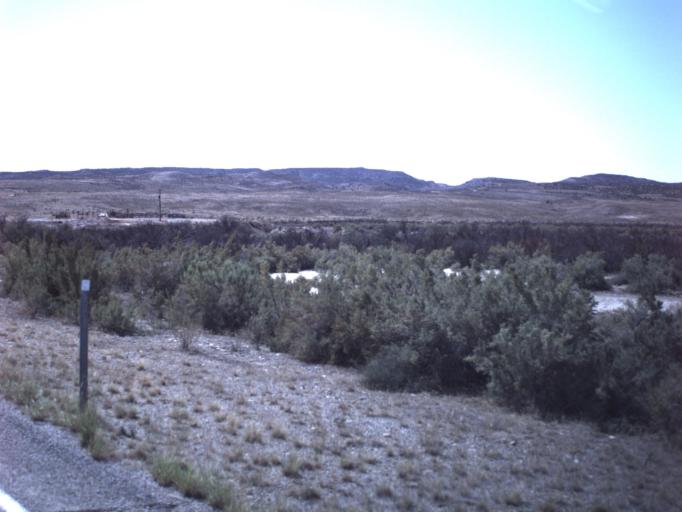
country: US
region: Utah
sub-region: Grand County
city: Moab
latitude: 38.8637
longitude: -109.2945
